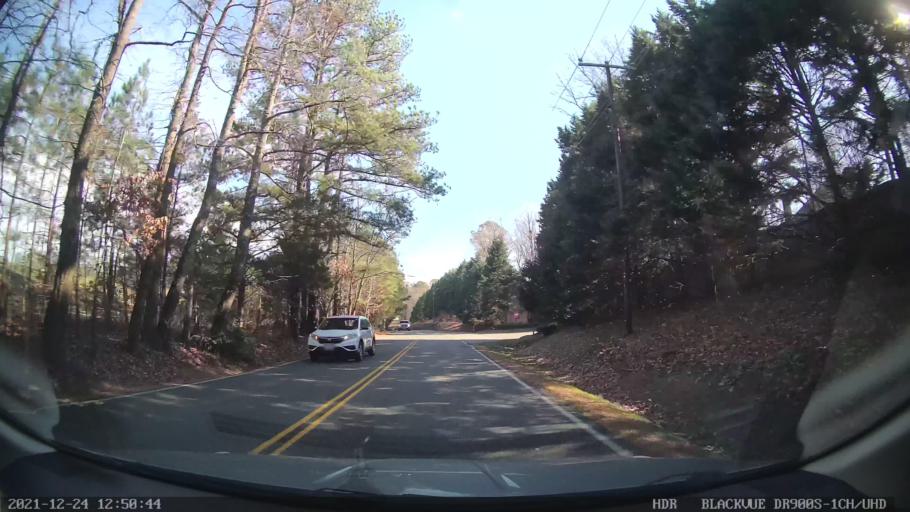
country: US
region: Virginia
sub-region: Henrico County
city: Short Pump
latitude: 37.6438
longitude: -77.5991
